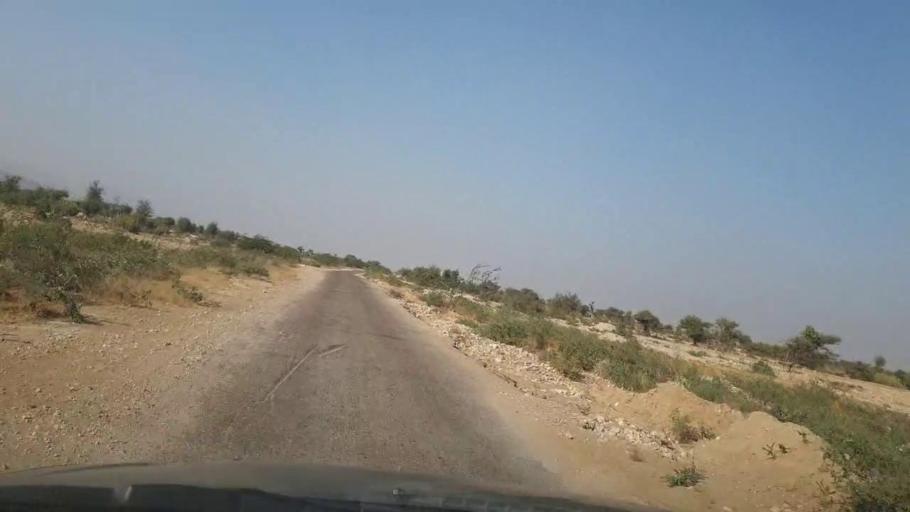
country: PK
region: Sindh
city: Jamshoro
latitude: 25.5687
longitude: 67.8243
